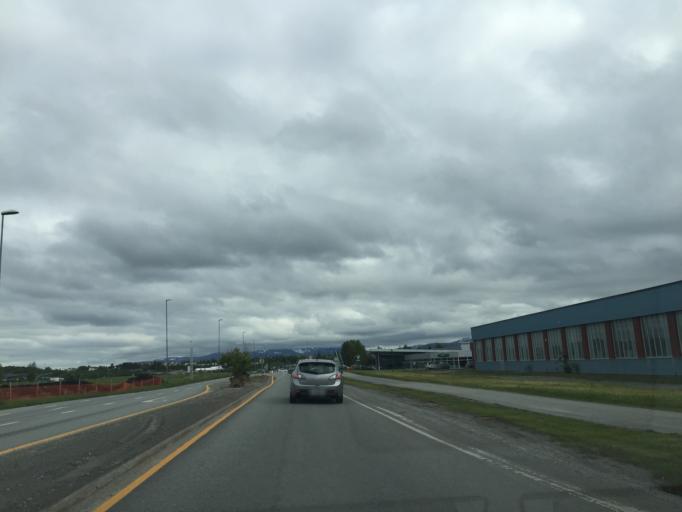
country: NO
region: Nordland
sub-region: Bodo
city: Bodo
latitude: 67.2828
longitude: 14.4150
